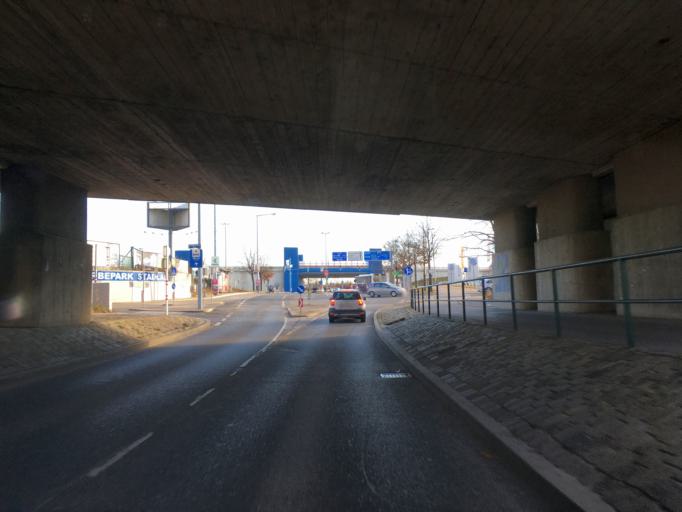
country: AT
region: Lower Austria
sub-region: Politischer Bezirk Wien-Umgebung
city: Gerasdorf bei Wien
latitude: 48.2418
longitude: 16.4585
